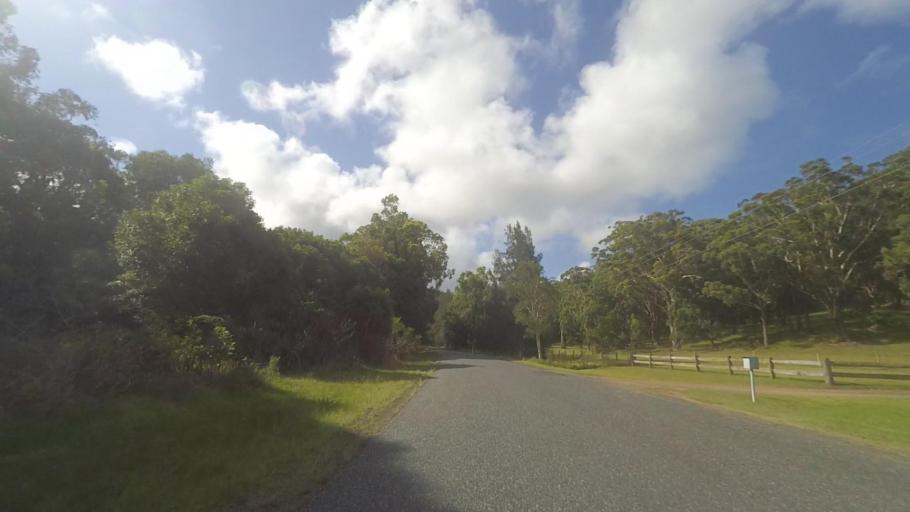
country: AU
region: New South Wales
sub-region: Great Lakes
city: Forster
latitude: -32.3983
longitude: 152.4592
